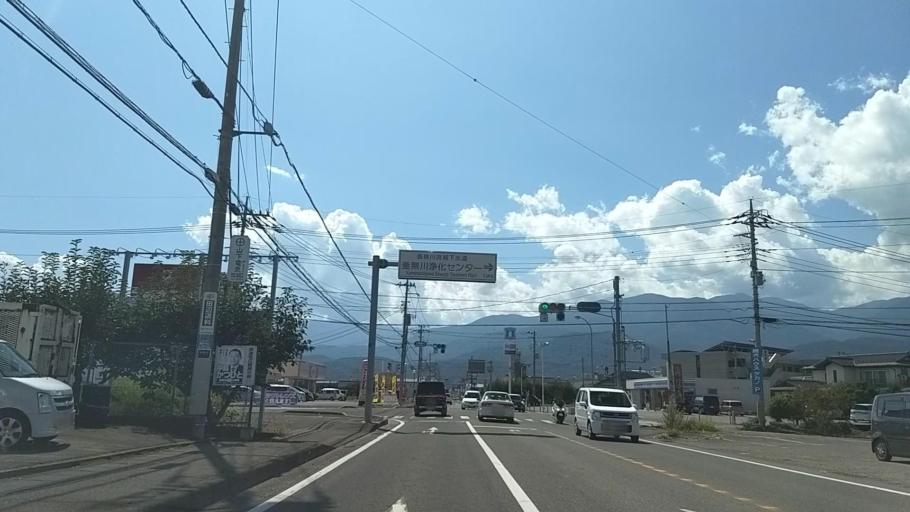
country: JP
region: Yamanashi
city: Ryuo
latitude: 35.5737
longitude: 138.4848
